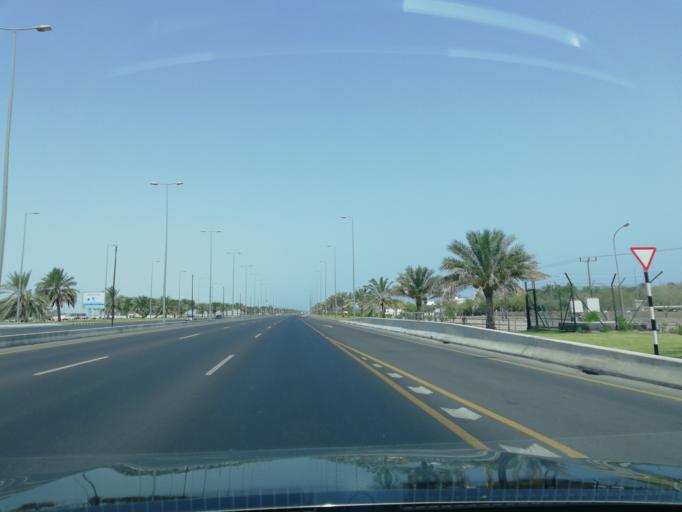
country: OM
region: Muhafazat Masqat
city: As Sib al Jadidah
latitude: 23.6817
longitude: 58.1087
